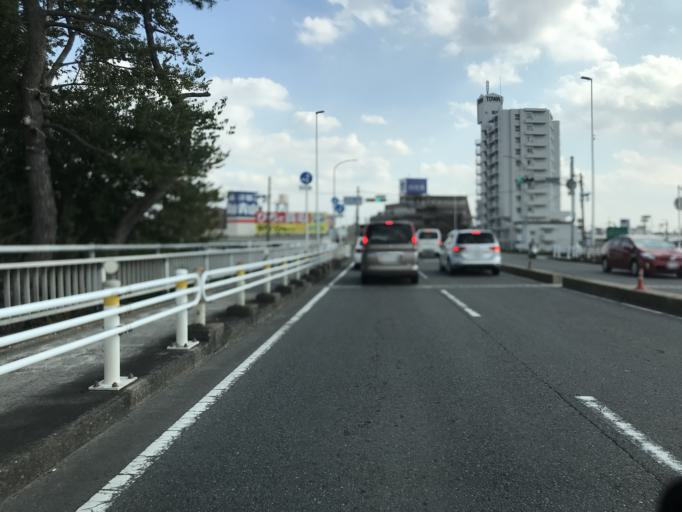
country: JP
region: Aichi
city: Nagoya-shi
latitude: 35.1788
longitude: 136.8472
